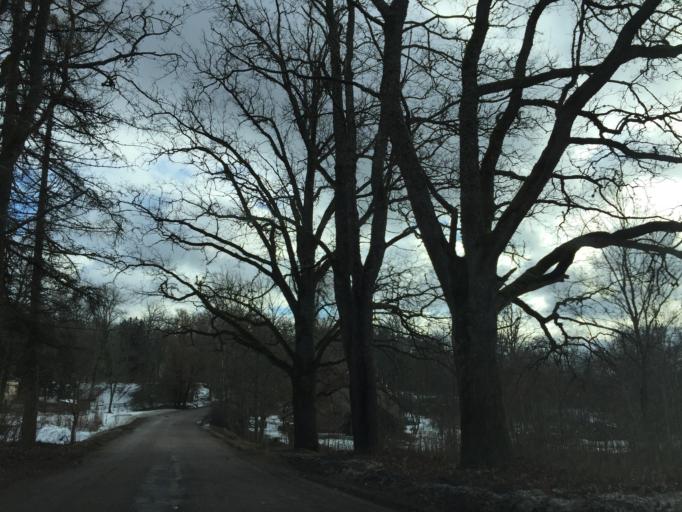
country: LV
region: Aloja
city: Aloja
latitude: 57.7752
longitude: 24.8121
